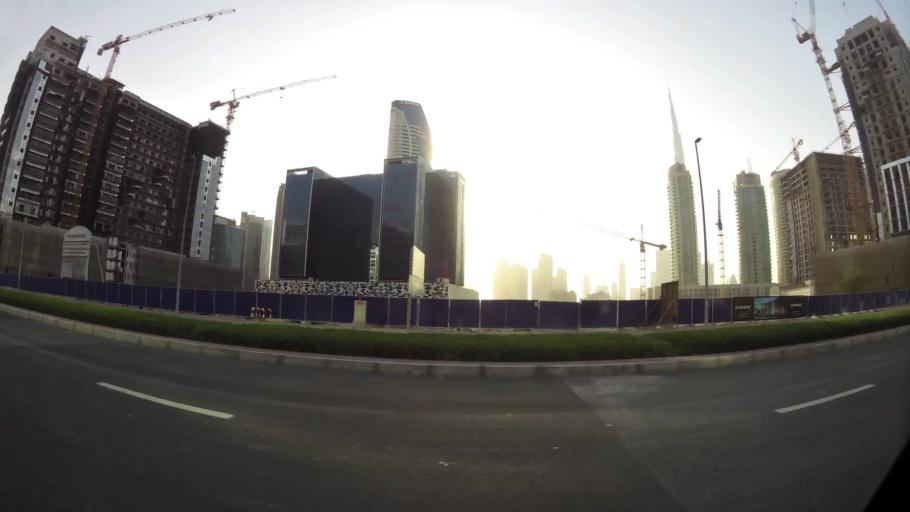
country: AE
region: Dubai
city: Dubai
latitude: 25.1873
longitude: 55.2836
